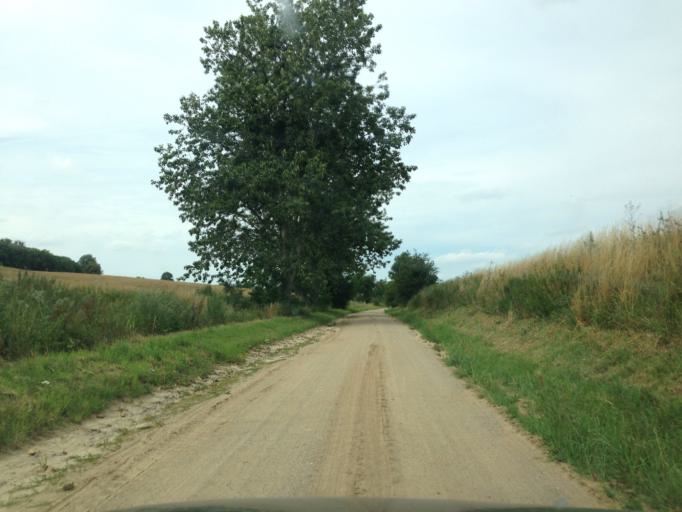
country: PL
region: Kujawsko-Pomorskie
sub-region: Powiat brodnicki
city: Brodnica
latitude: 53.2841
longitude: 19.4271
